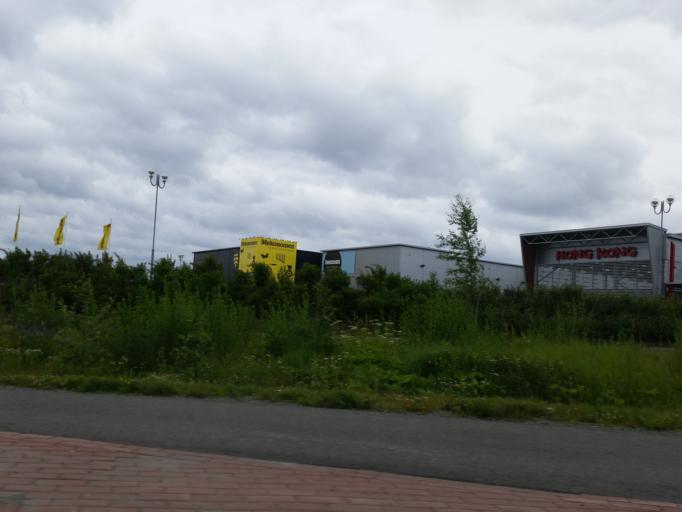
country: FI
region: Northern Savo
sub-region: Kuopio
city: Kuopio
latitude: 62.8744
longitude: 27.6227
